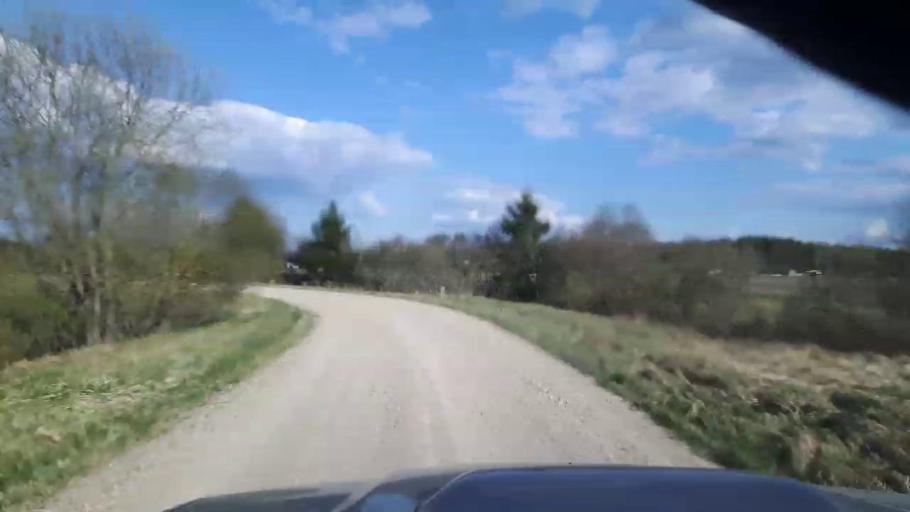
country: EE
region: Paernumaa
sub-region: Tootsi vald
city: Tootsi
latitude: 58.4140
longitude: 24.8437
